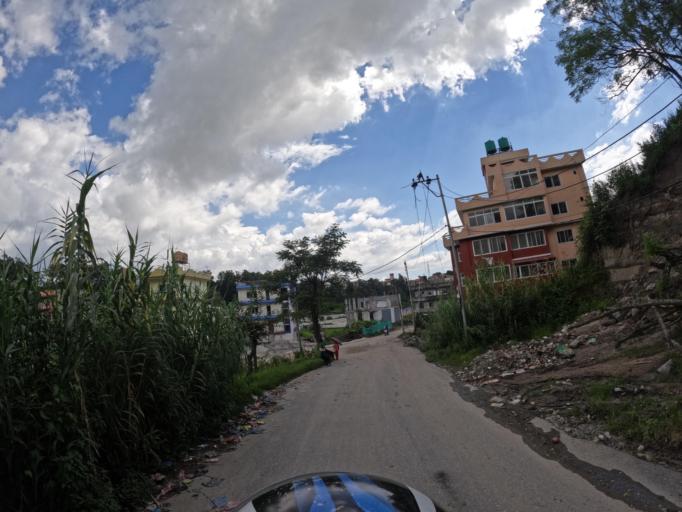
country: NP
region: Central Region
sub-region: Bagmati Zone
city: Kathmandu
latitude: 27.7660
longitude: 85.3270
